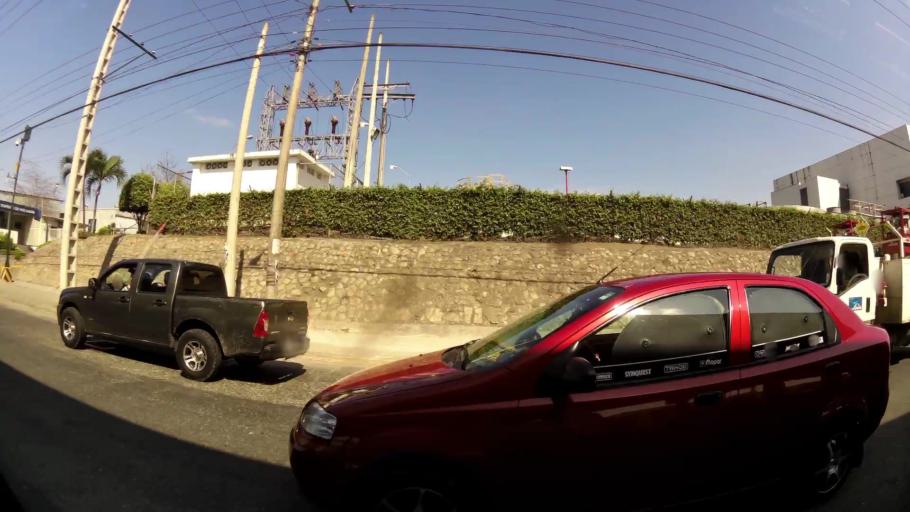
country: EC
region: Guayas
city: Guayaquil
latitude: -2.1222
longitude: -79.9315
